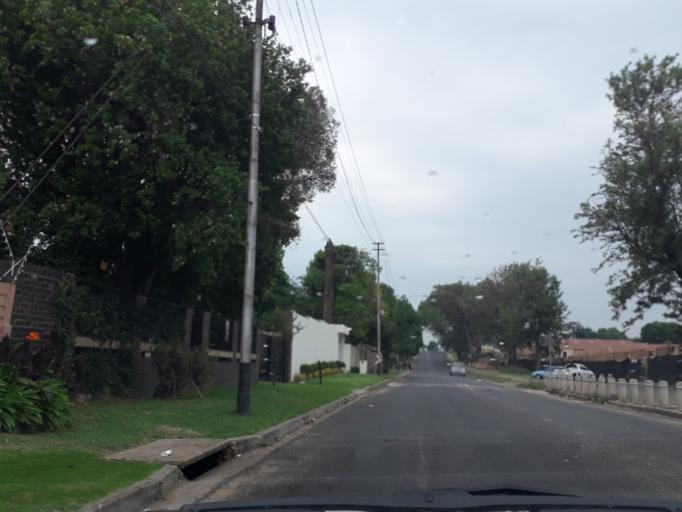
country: ZA
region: Gauteng
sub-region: City of Johannesburg Metropolitan Municipality
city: Johannesburg
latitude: -26.1464
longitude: 28.0981
